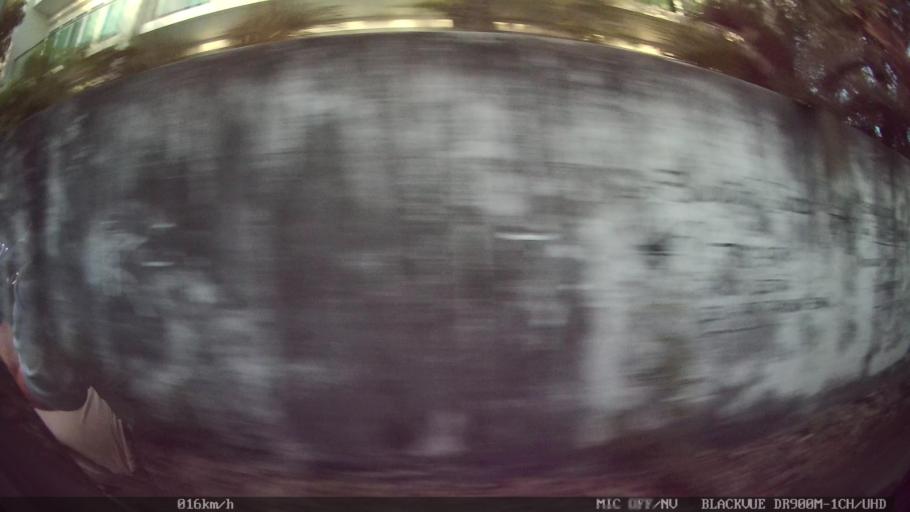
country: ID
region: Bali
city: Bualu
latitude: -8.7599
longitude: 115.2196
